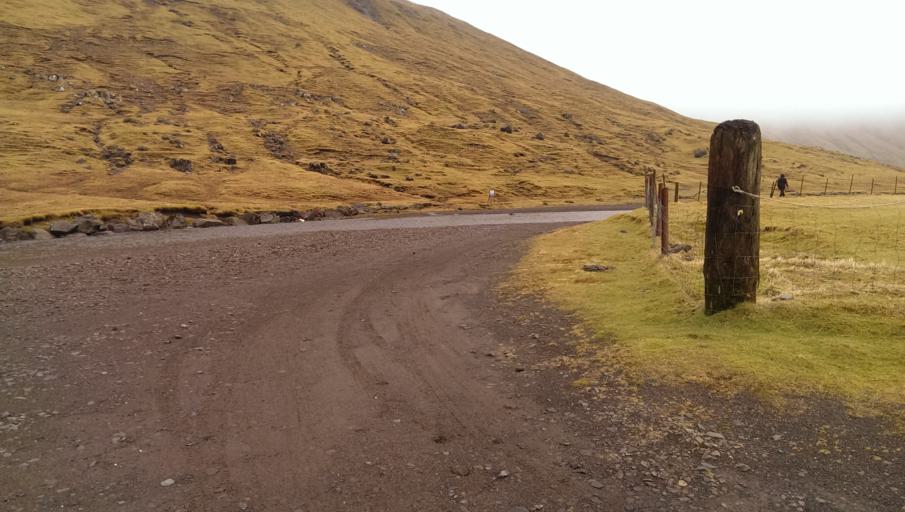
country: FO
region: Streymoy
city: Kollafjordhur
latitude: 62.1325
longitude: -7.0232
